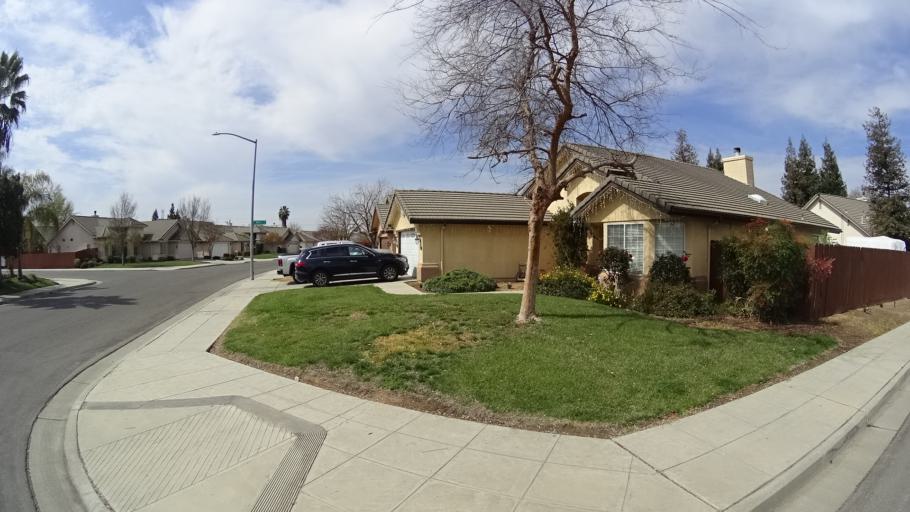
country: US
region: California
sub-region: Fresno County
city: West Park
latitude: 36.8203
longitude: -119.8732
